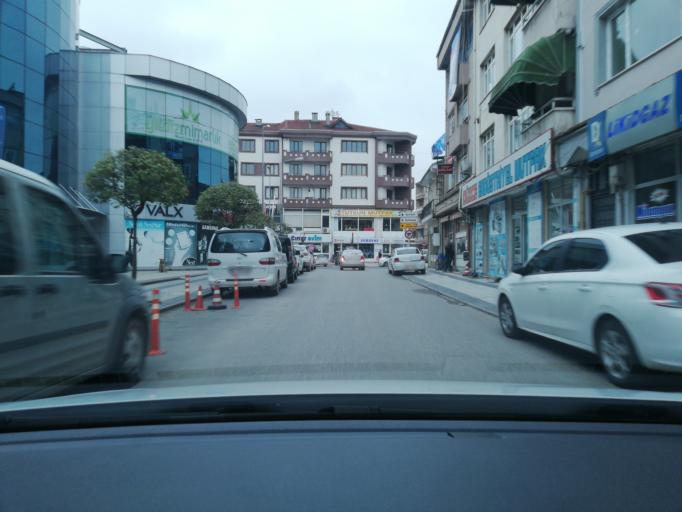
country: TR
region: Duzce
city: Duzce
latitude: 40.8377
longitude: 31.1643
